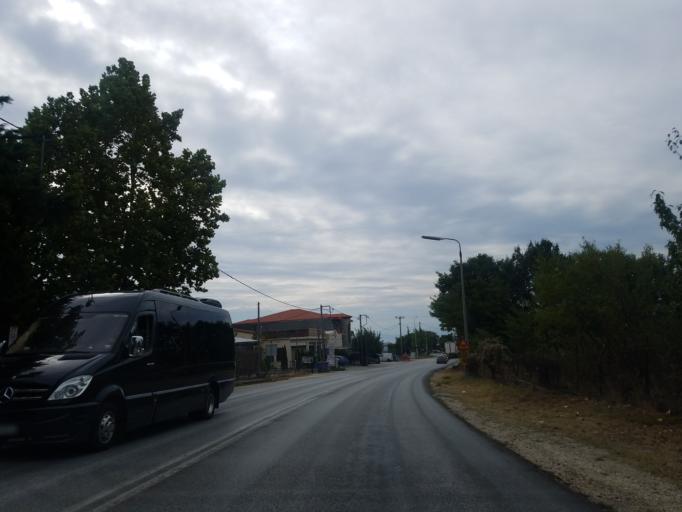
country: GR
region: Thessaly
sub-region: Trikala
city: Kalampaka
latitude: 39.6979
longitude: 21.6398
